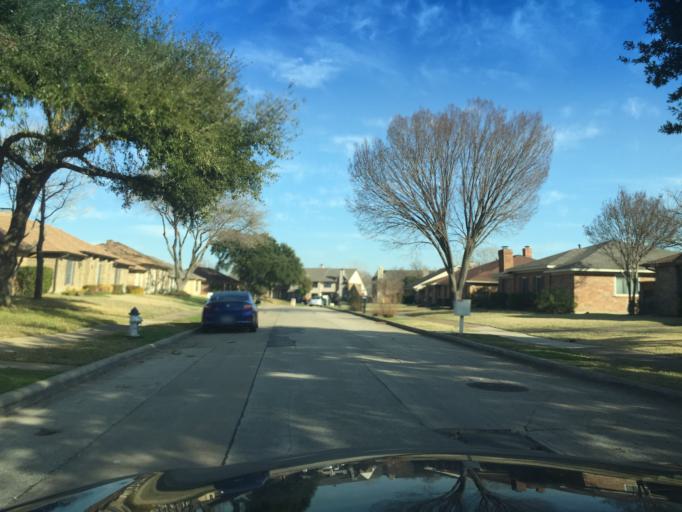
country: US
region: Texas
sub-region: Dallas County
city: Carrollton
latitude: 32.9796
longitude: -96.8803
